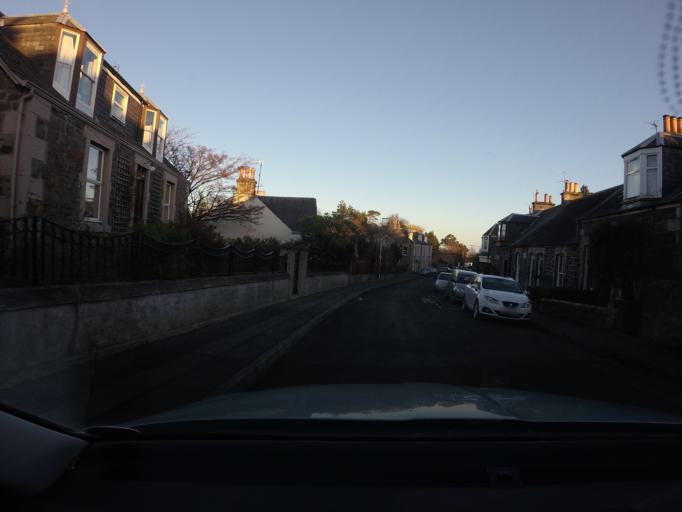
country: GB
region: Scotland
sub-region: Fife
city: Tayport
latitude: 56.4466
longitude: -2.8820
